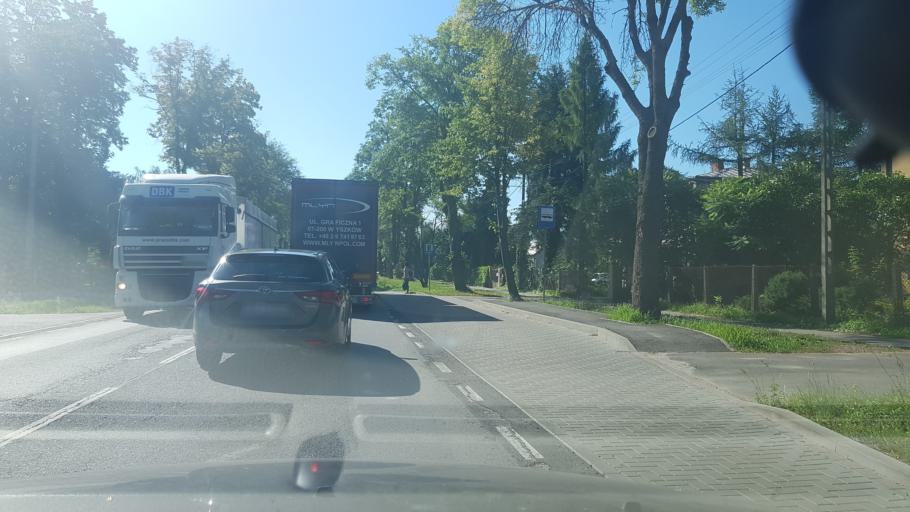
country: PL
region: Masovian Voivodeship
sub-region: Powiat wegrowski
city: Lochow
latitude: 52.5331
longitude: 21.6772
